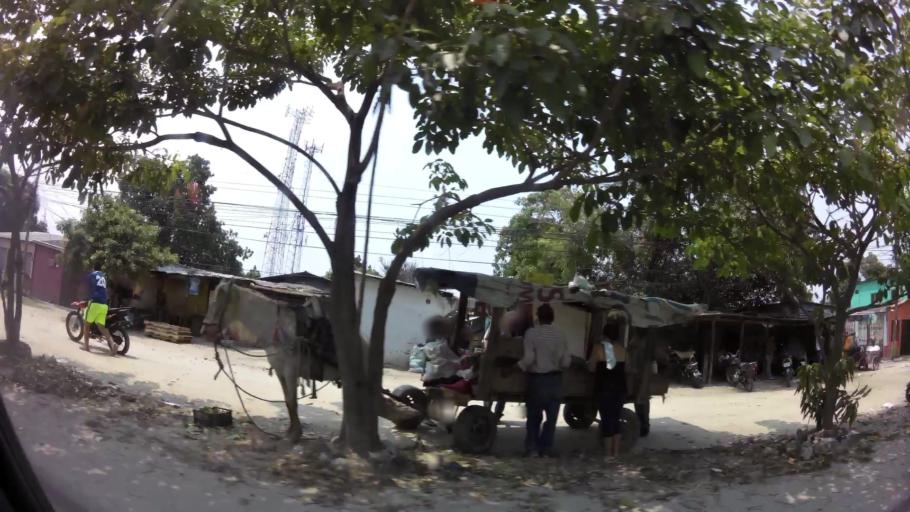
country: HN
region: Cortes
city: San Pedro Sula
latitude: 15.4776
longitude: -87.9845
